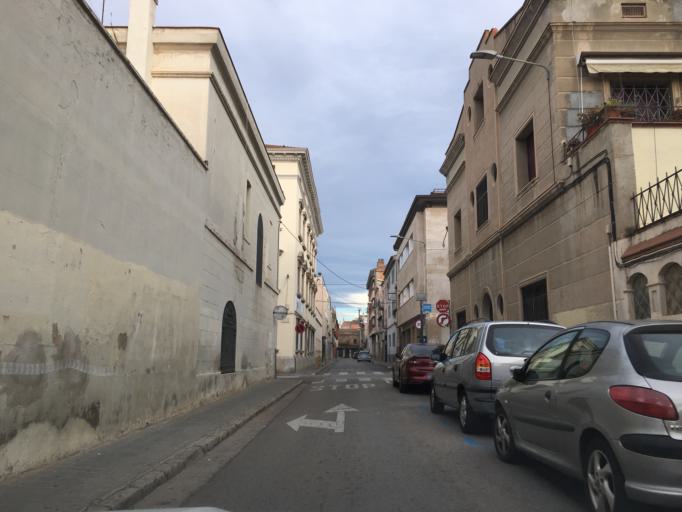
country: ES
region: Catalonia
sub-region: Provincia de Barcelona
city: Sabadell
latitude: 41.5497
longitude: 2.1069
